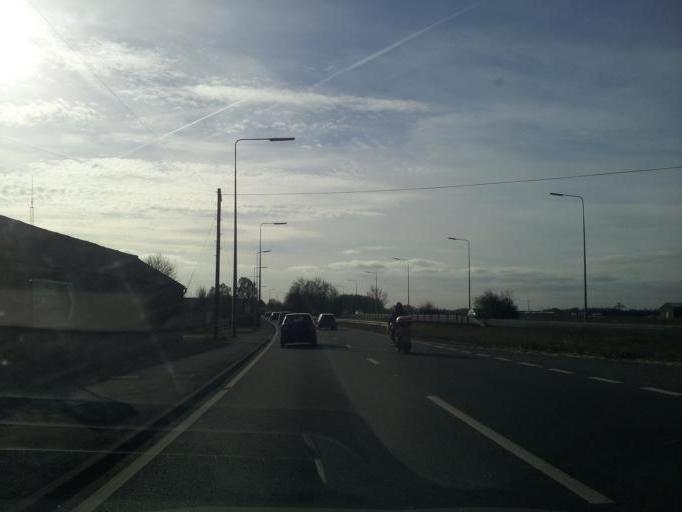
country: GB
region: England
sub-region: Central Bedfordshire
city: Biggleswade
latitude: 52.1002
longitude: -0.2764
